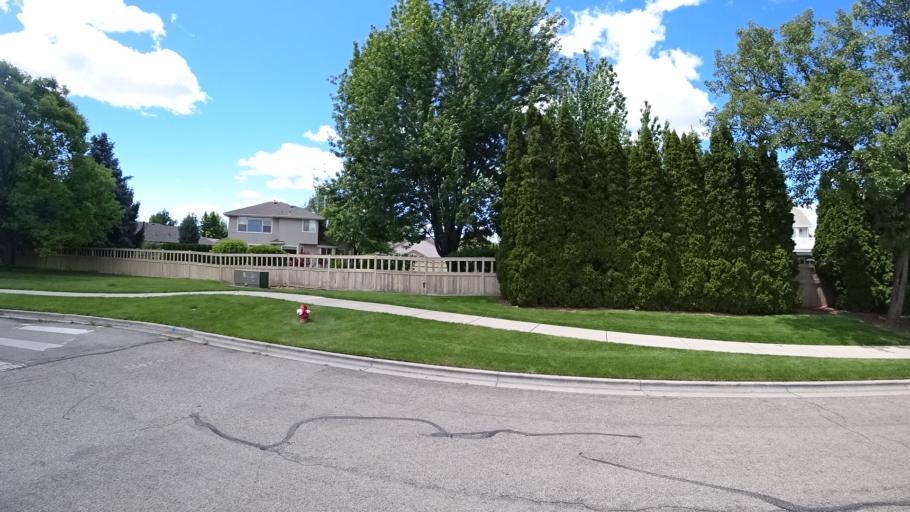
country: US
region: Idaho
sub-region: Ada County
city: Eagle
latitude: 43.6599
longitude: -116.3456
